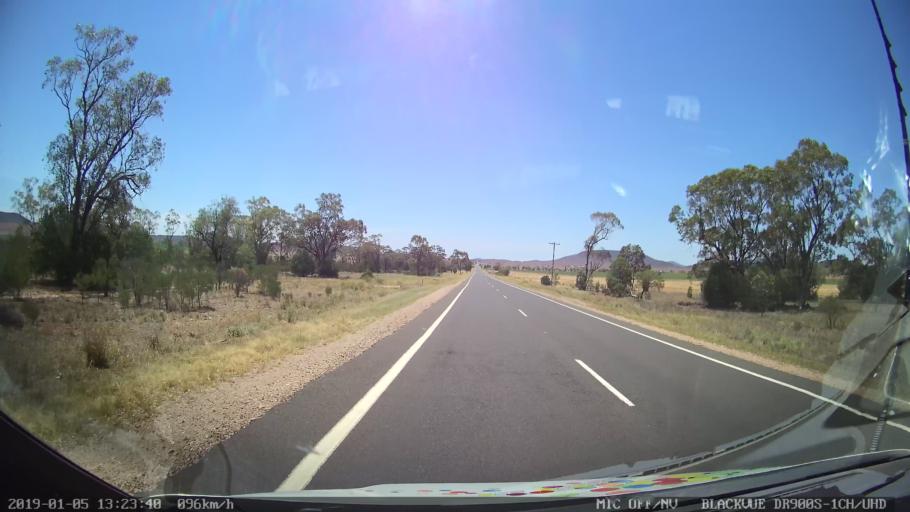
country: AU
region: New South Wales
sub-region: Gunnedah
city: Gunnedah
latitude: -31.0760
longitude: 149.9783
